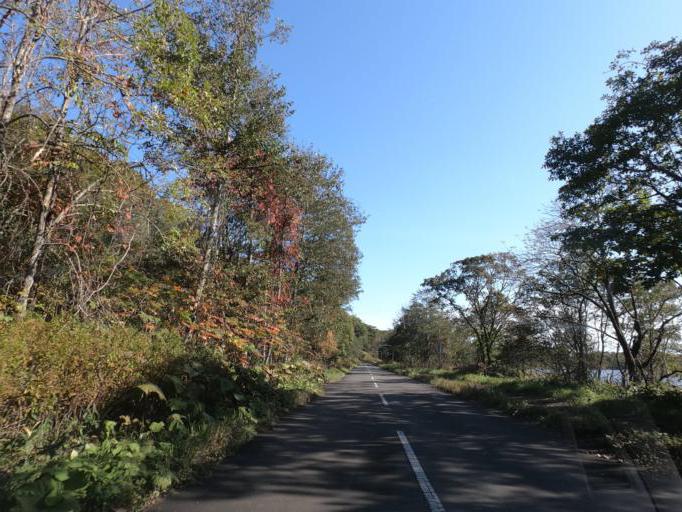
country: JP
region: Hokkaido
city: Obihiro
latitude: 42.6089
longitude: 143.5469
